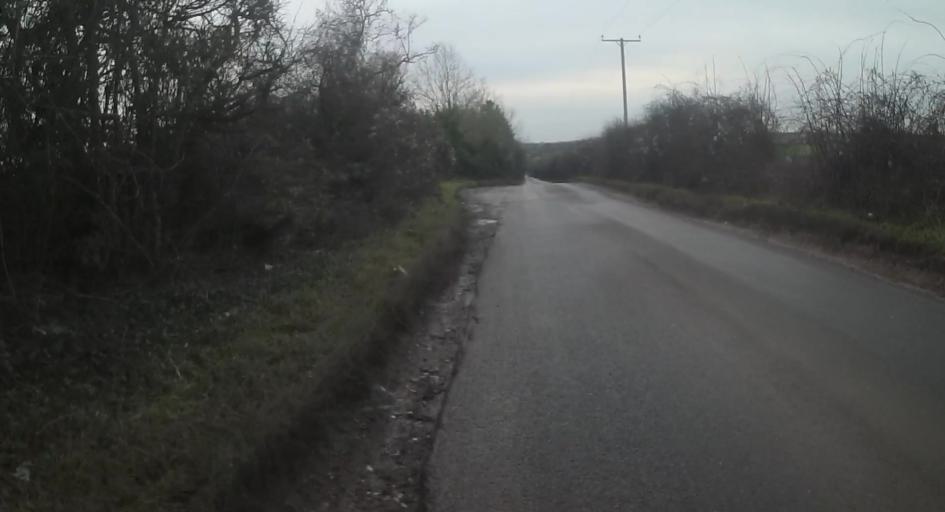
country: GB
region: England
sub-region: Hampshire
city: Overton
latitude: 51.2458
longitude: -1.3545
